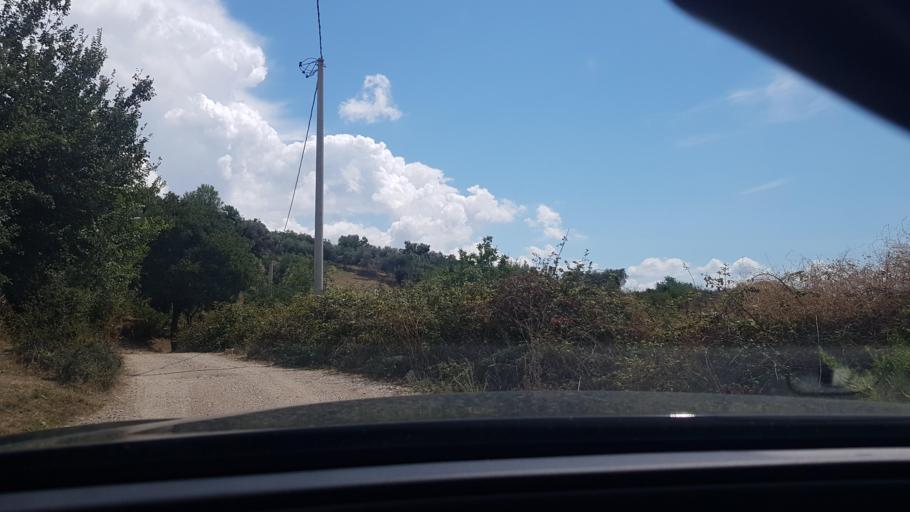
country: AL
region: Tirane
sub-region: Rrethi i Kavajes
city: Golem
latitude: 41.2874
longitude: 19.5487
